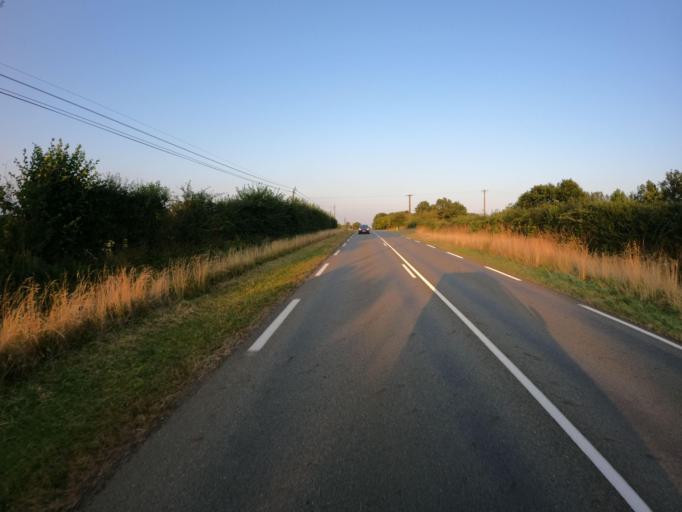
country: FR
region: Pays de la Loire
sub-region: Departement de la Mayenne
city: Meslay-du-Maine
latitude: 47.8706
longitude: -0.4744
